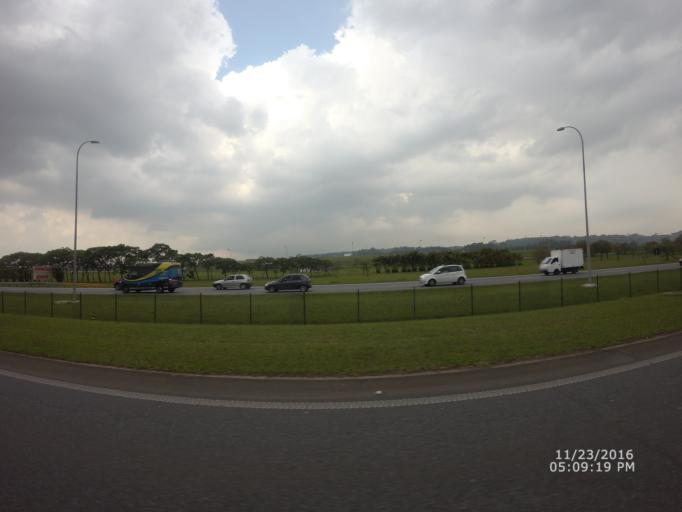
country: BR
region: Sao Paulo
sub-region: Guarulhos
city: Guarulhos
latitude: -23.4379
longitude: -46.4942
